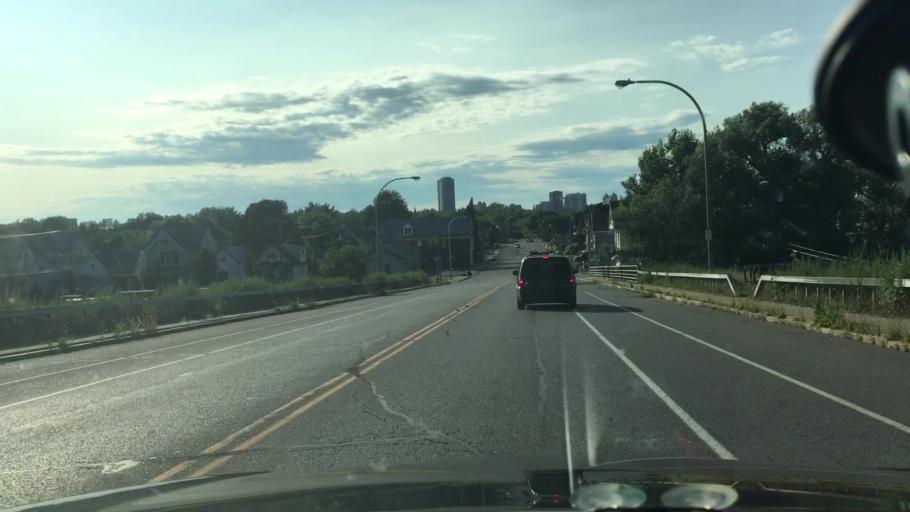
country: US
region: New York
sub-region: Erie County
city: Buffalo
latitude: 42.8654
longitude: -78.8466
